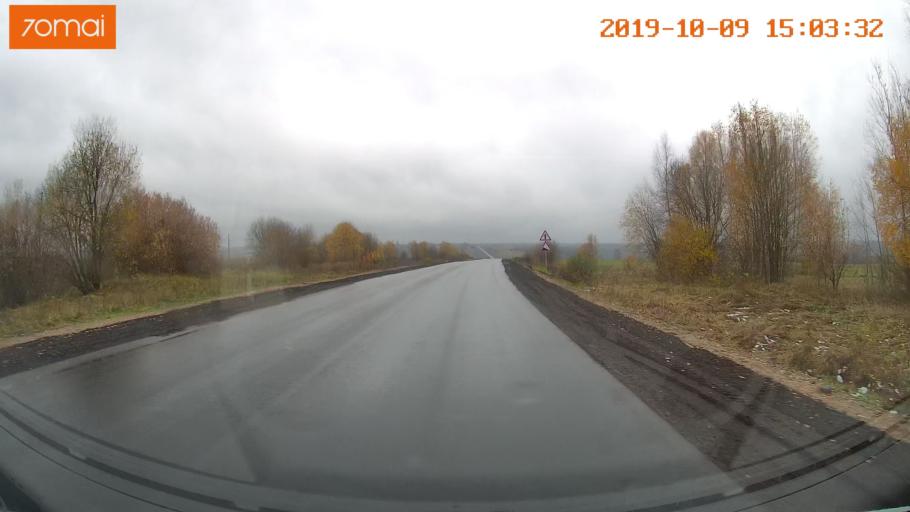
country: RU
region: Kostroma
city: Chistyye Bory
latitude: 58.2701
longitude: 41.6752
